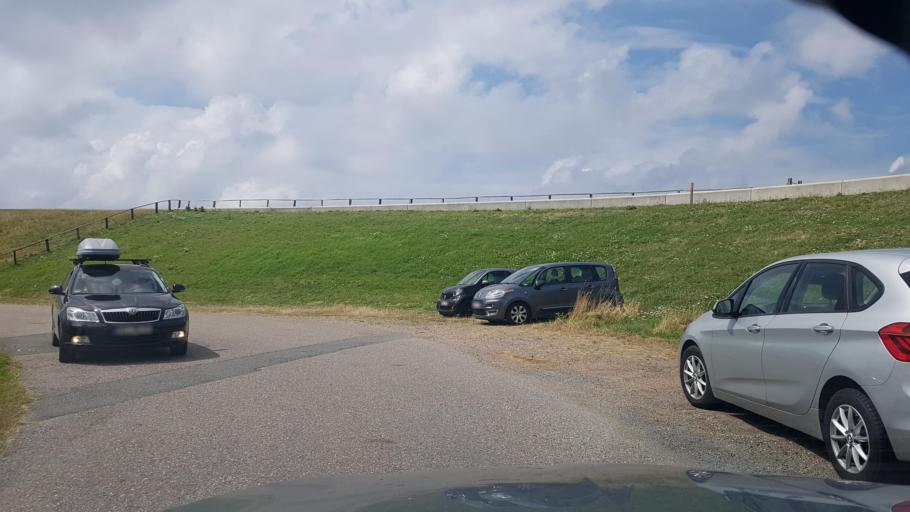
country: DE
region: Schleswig-Holstein
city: Elisabeth-Sophien-Koog
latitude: 54.4965
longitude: 8.8074
